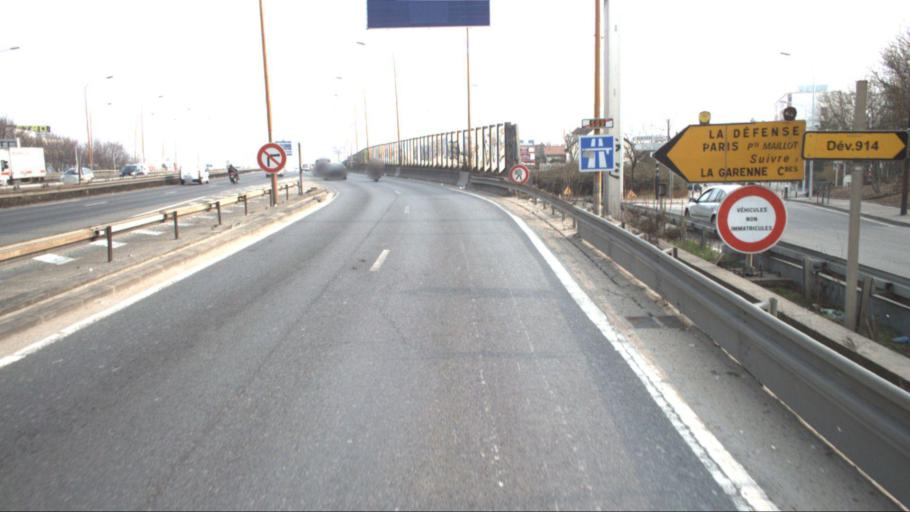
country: FR
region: Ile-de-France
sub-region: Departement du Val-d'Oise
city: Bezons
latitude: 48.9082
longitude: 2.2139
